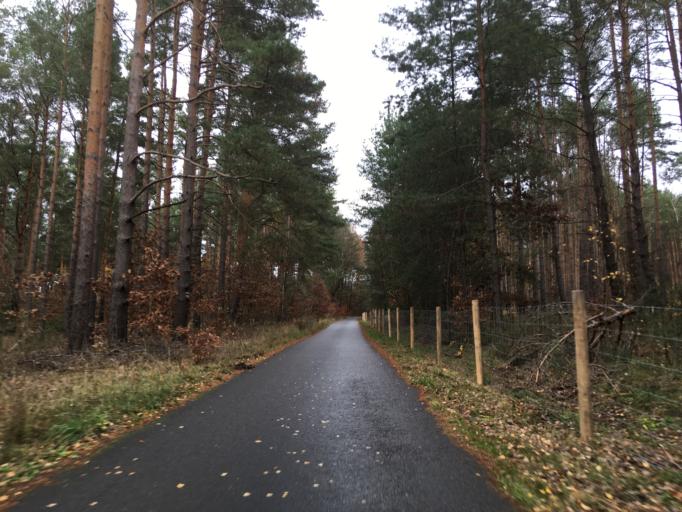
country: DE
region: Brandenburg
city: Jamlitz
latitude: 52.0325
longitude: 14.4683
